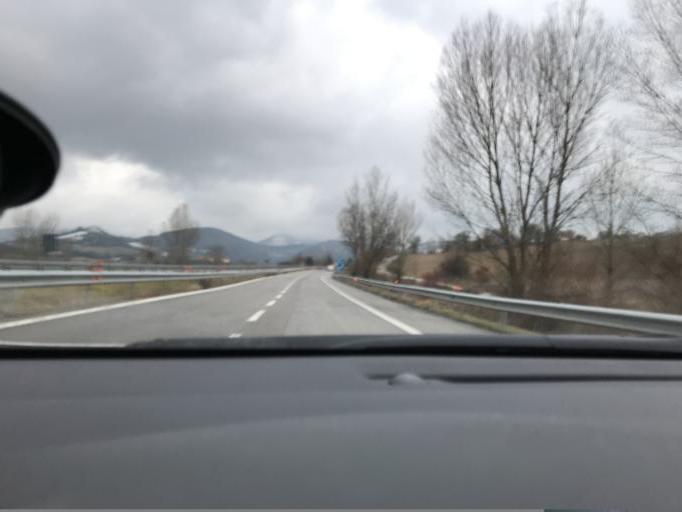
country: IT
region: The Marches
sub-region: Provincia di Ancona
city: Fabriano
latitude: 43.3308
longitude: 12.9267
